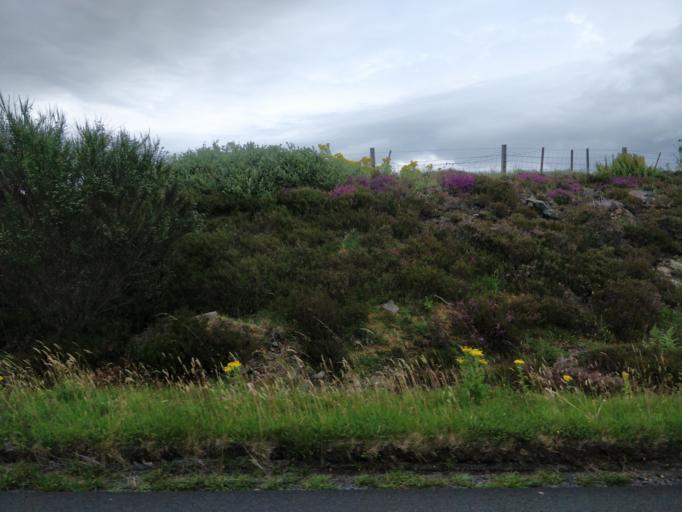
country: GB
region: Scotland
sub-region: Highland
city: Isle of Skye
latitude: 57.3682
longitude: -6.4454
